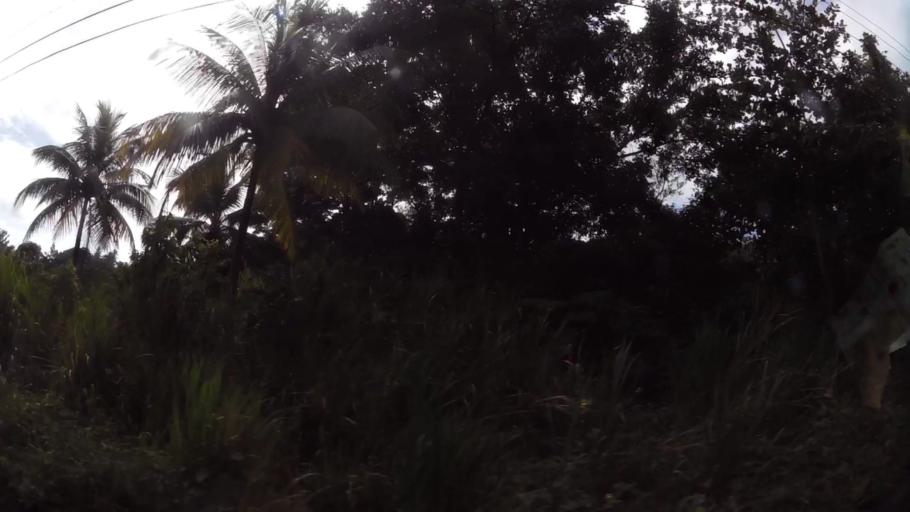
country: DM
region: Saint David
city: Castle Bruce
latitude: 15.4654
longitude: -61.2522
